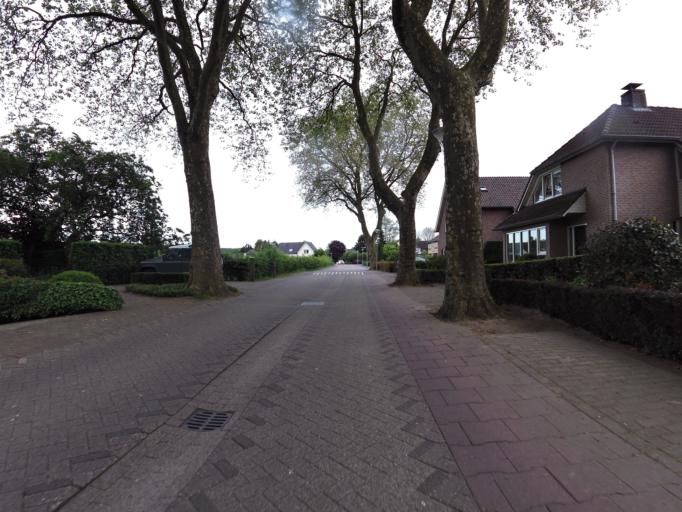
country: NL
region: Gelderland
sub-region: Gemeente Montferland
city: s-Heerenberg
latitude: 51.9040
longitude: 6.1908
